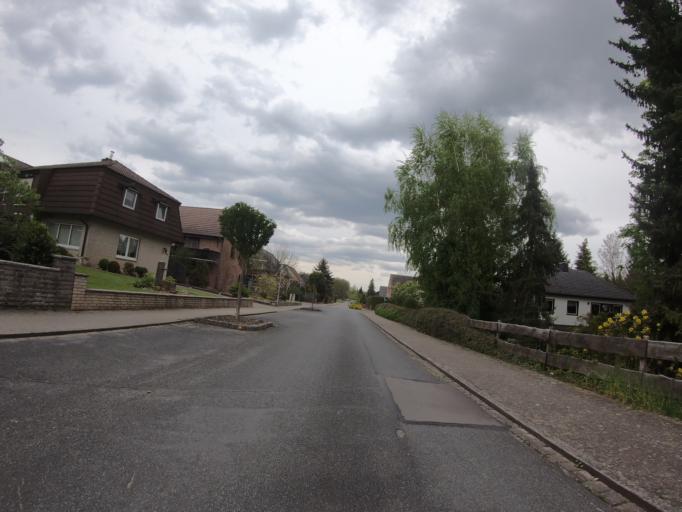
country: DE
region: Lower Saxony
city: Wasbuttel
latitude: 52.4169
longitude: 10.5988
